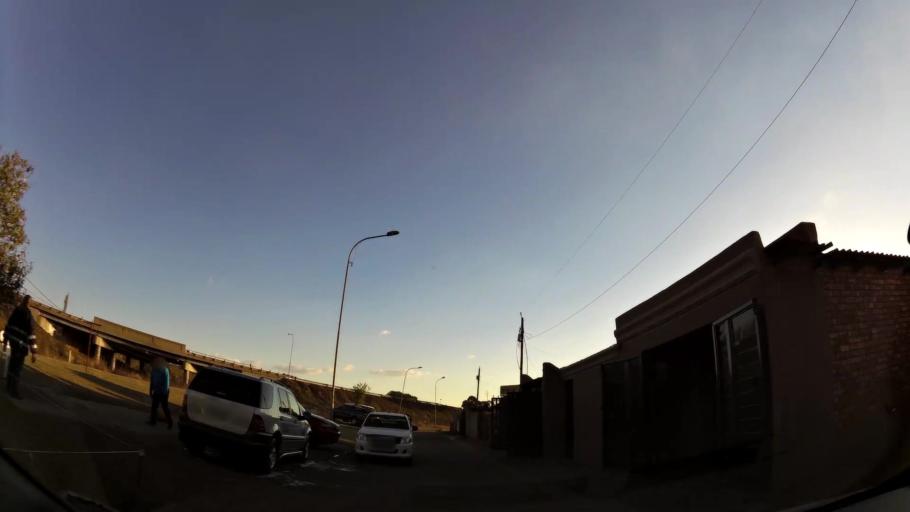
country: ZA
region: Mpumalanga
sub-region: Nkangala District Municipality
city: Witbank
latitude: -25.8824
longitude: 29.1928
